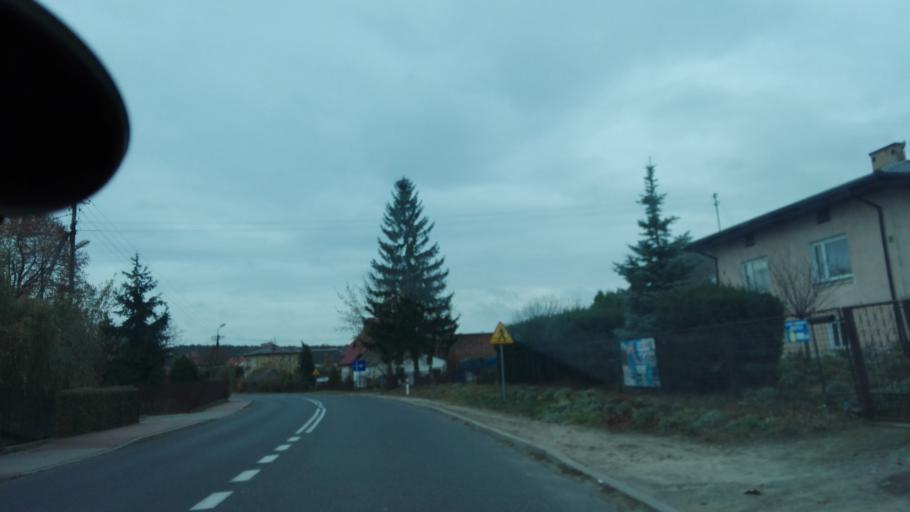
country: PL
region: Lublin Voivodeship
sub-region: Powiat pulawski
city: Pulawy
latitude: 51.4343
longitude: 21.9121
